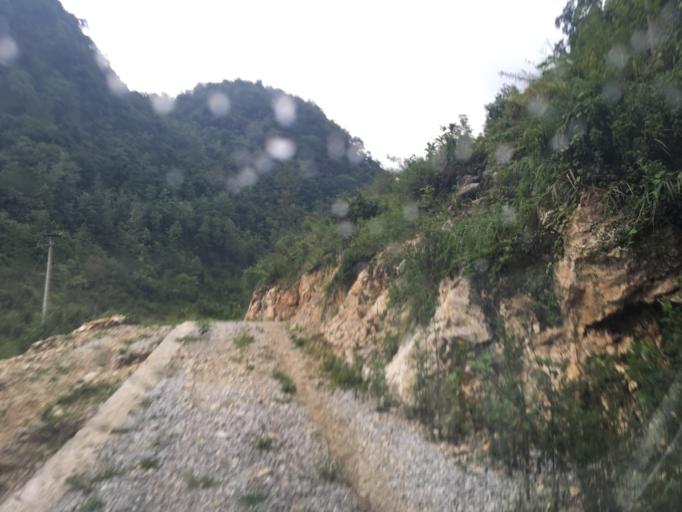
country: CN
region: Guangxi Zhuangzu Zizhiqu
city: Xinzhou
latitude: 25.2247
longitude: 105.6282
